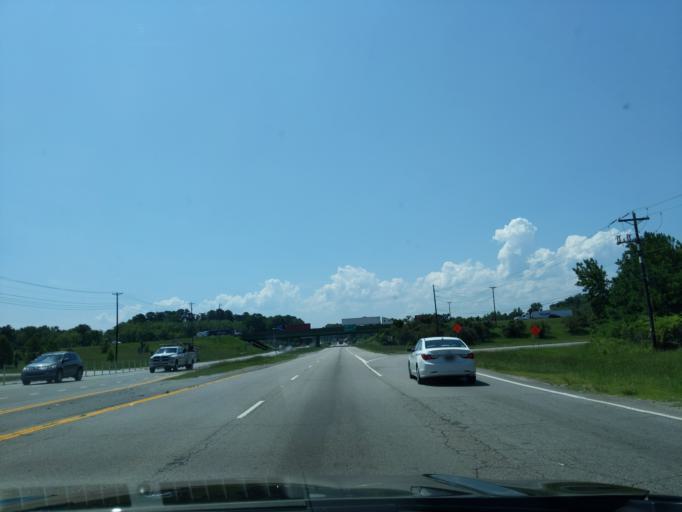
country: US
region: South Carolina
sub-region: Richland County
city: Columbia
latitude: 33.9526
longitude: -80.9914
